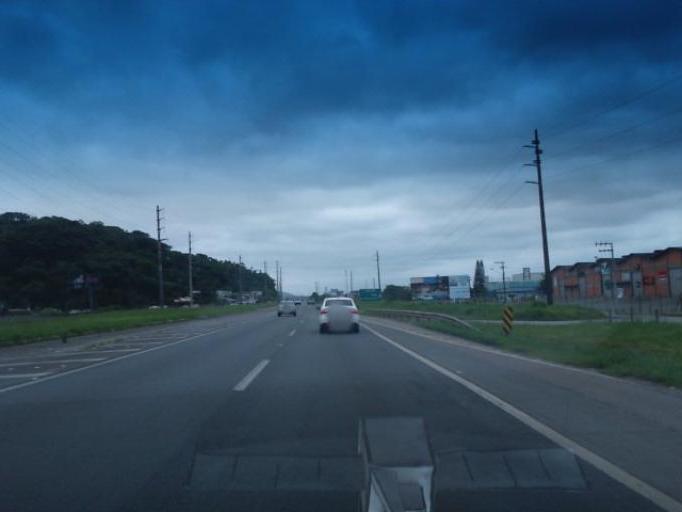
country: BR
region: Santa Catarina
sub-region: Itajai
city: Itajai
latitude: -26.9030
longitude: -48.7159
